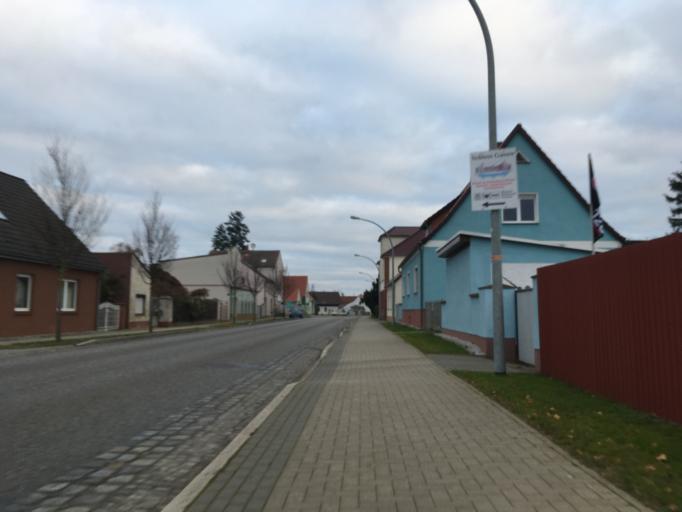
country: DE
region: Brandenburg
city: Seelow
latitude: 52.5688
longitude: 14.3532
